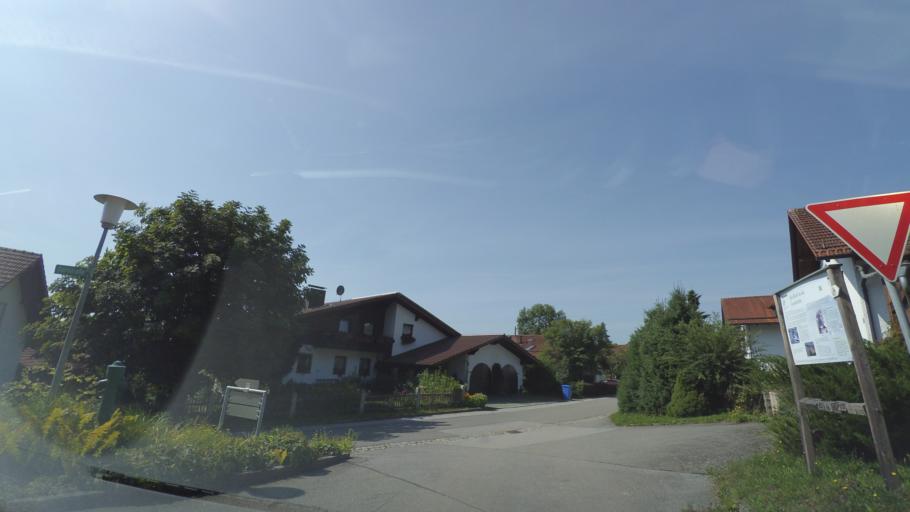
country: DE
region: Bavaria
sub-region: Lower Bavaria
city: Geiersthal
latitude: 49.0581
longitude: 12.9708
